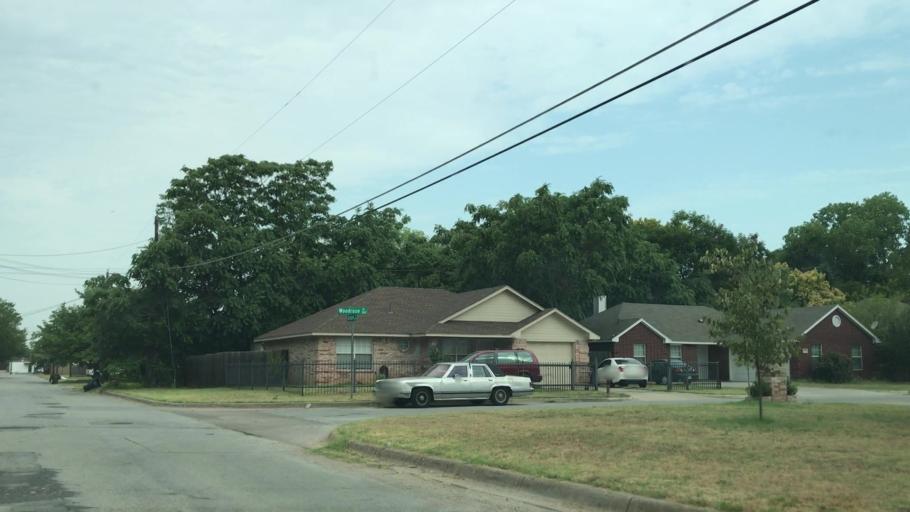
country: US
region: Texas
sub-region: Tarrant County
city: Haltom City
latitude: 32.7672
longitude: -97.2847
